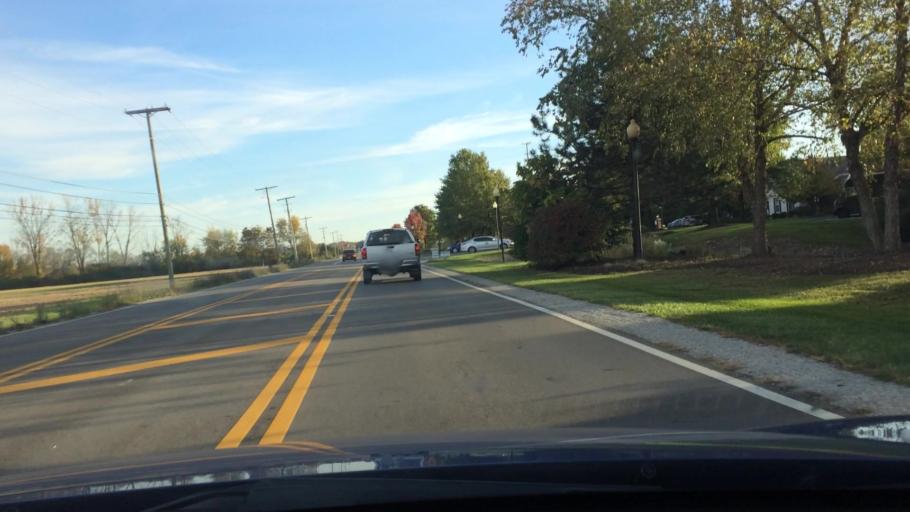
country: US
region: Ohio
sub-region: Franklin County
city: Hilliard
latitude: 40.0714
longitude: -83.1496
